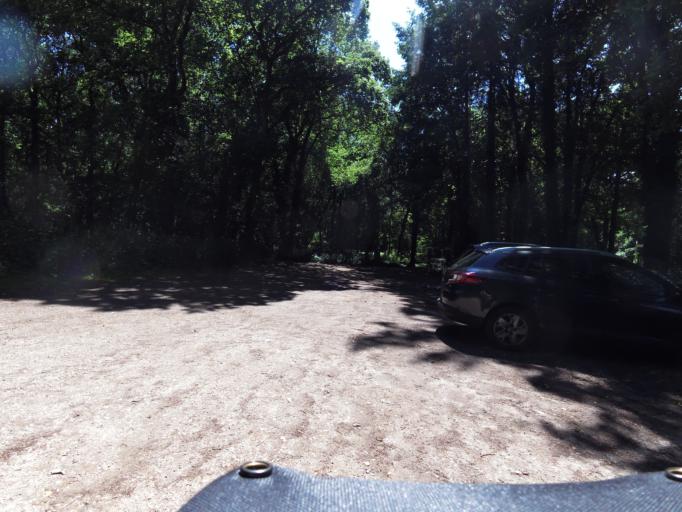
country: NL
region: Overijssel
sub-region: Gemeente Twenterand
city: Den Ham
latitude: 52.4946
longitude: 6.4300
